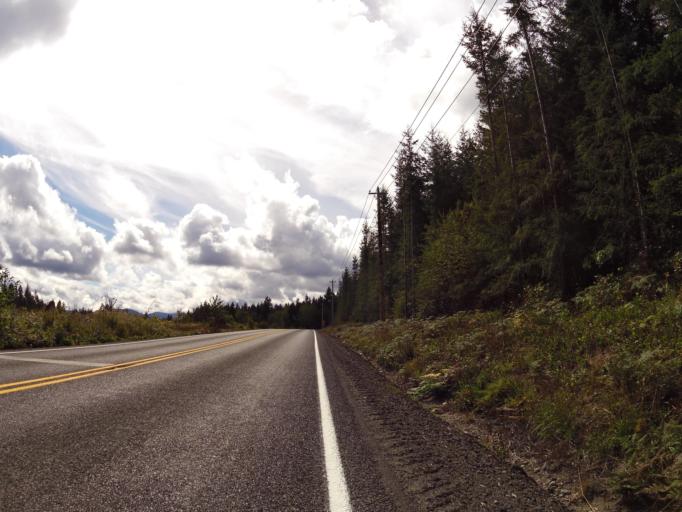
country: US
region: Washington
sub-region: Mason County
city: Shelton
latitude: 47.1451
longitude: -123.0826
